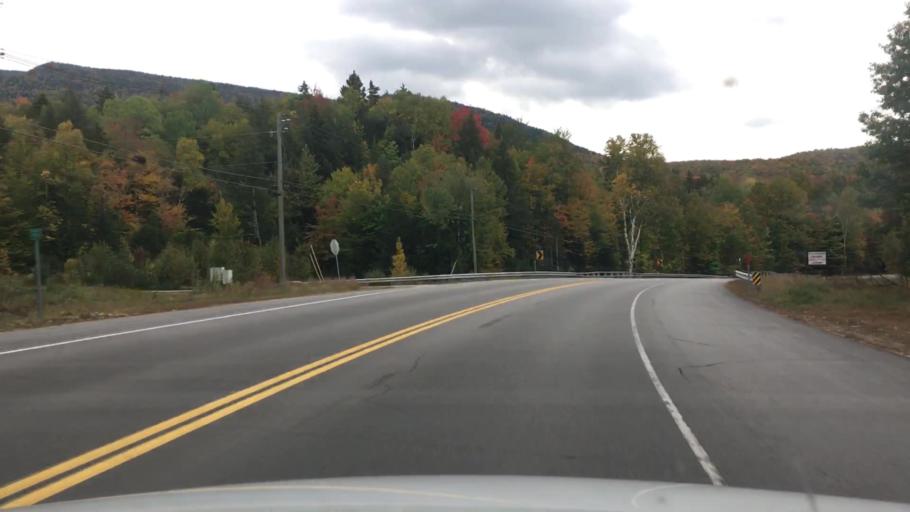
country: US
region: New Hampshire
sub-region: Coos County
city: Gorham
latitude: 44.3467
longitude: -71.1954
